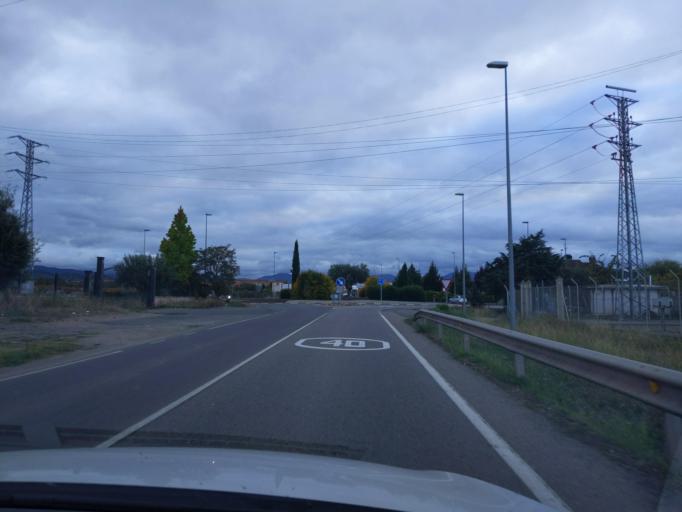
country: ES
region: La Rioja
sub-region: Provincia de La Rioja
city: Najera
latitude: 42.4250
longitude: -2.7207
